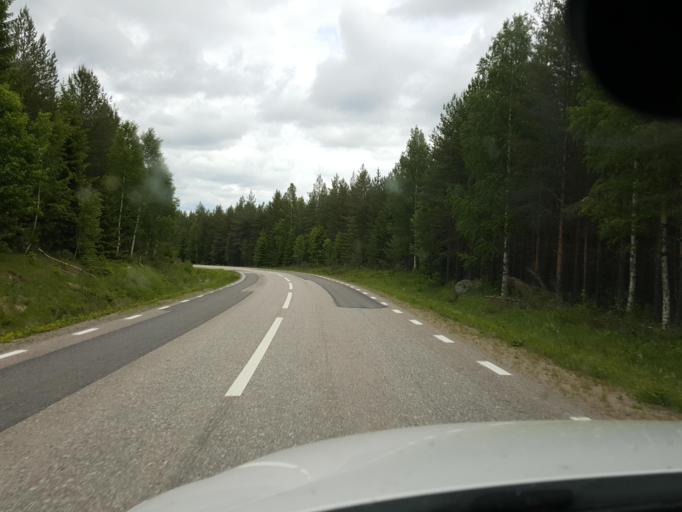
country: SE
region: Gaevleborg
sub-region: Ljusdals Kommun
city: Farila
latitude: 61.7678
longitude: 15.5873
